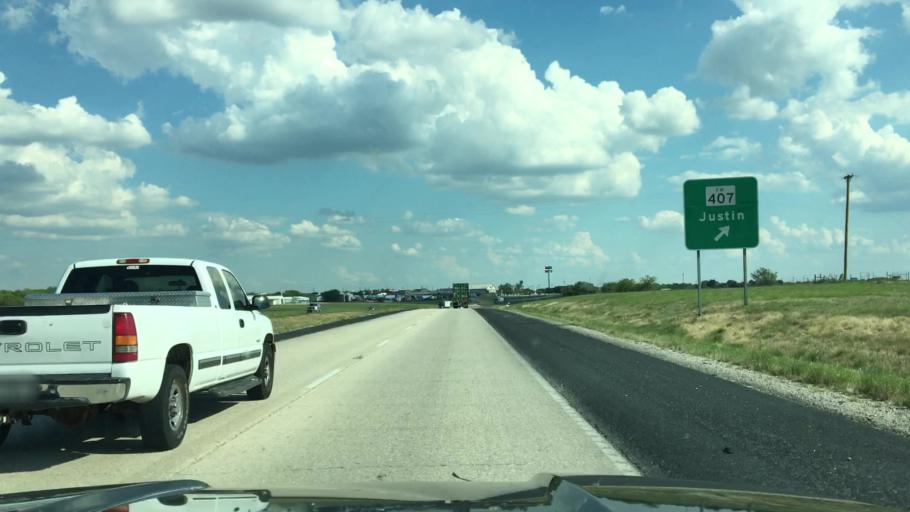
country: US
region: Texas
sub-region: Wise County
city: New Fairview
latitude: 33.1084
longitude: -97.4758
